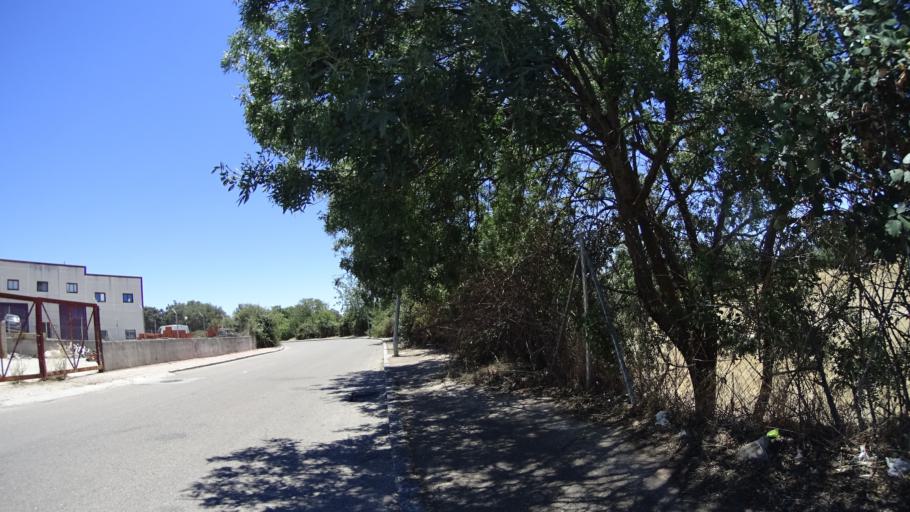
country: ES
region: Madrid
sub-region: Provincia de Madrid
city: Alpedrete
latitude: 40.6592
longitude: -4.0179
